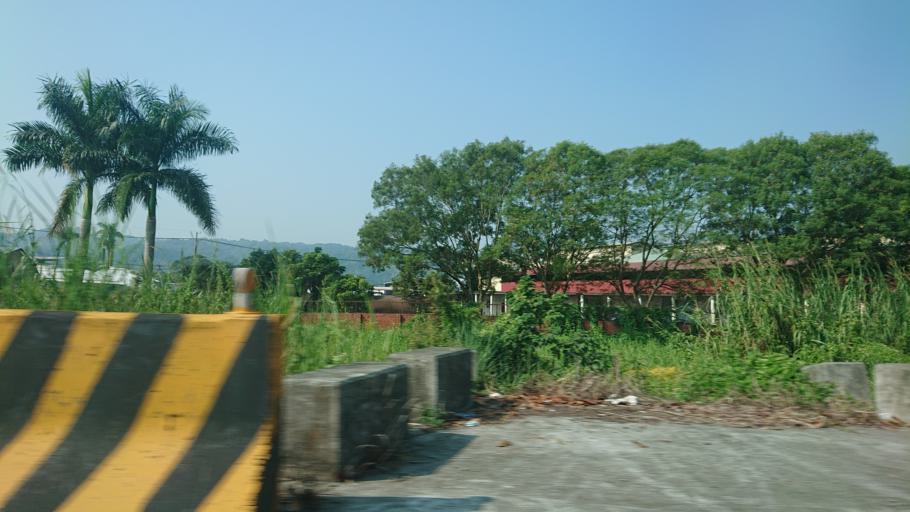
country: TW
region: Taiwan
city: Lugu
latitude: 23.7656
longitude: 120.6597
